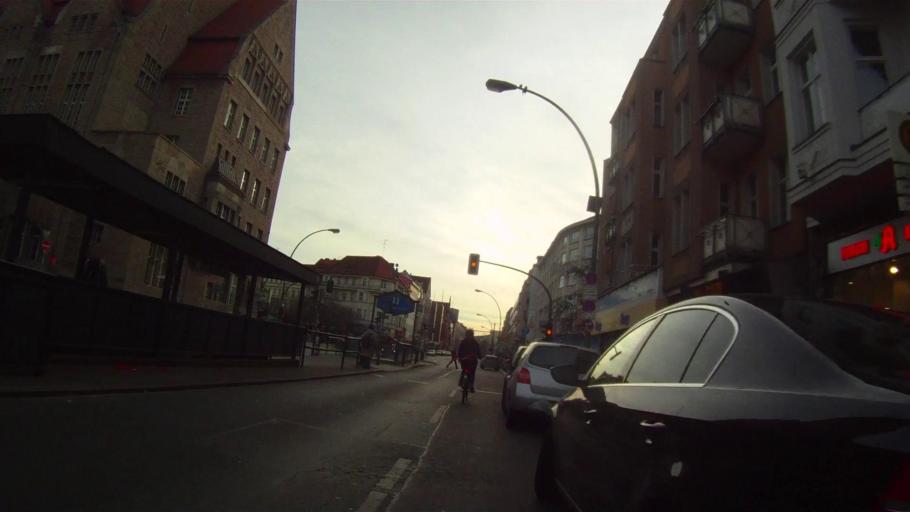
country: DE
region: Berlin
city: Berlin Treptow
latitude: 52.4816
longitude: 13.4341
